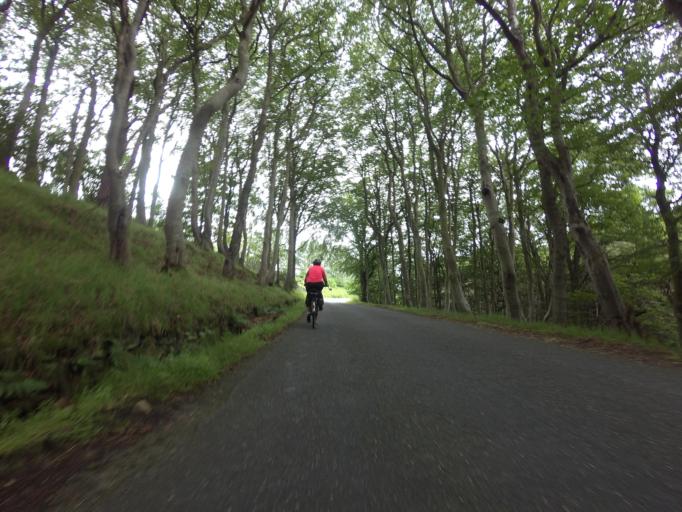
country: GB
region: Scotland
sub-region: Aberdeenshire
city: Portsoy
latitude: 57.6730
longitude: -2.7189
